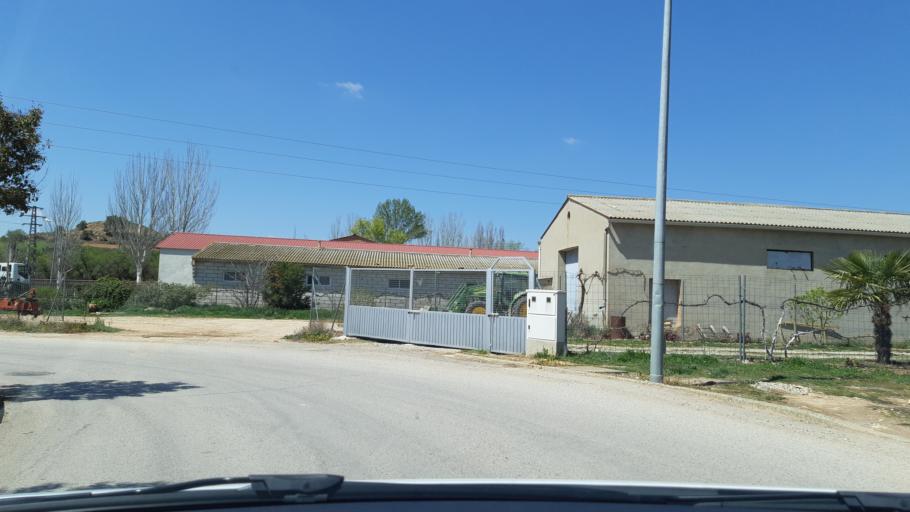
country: ES
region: Castille-La Mancha
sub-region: Provincia de Guadalajara
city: Cifuentes
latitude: 40.7881
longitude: -2.6228
